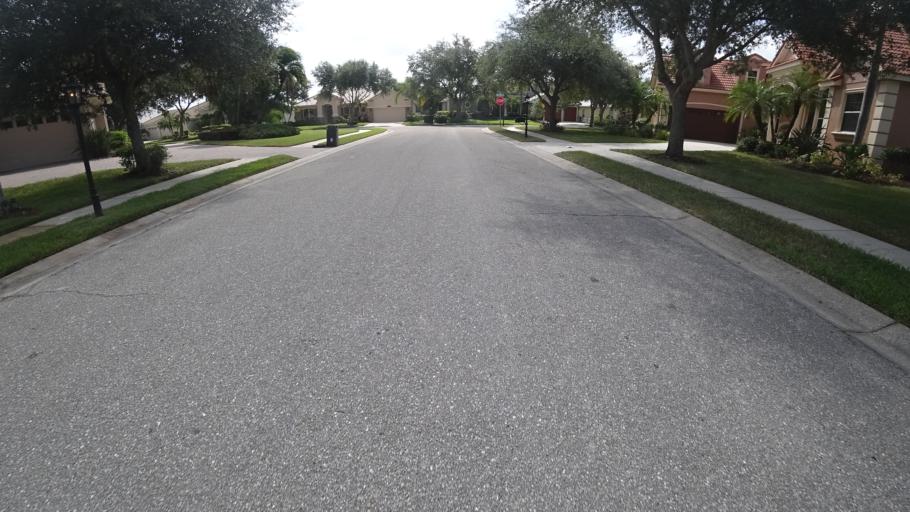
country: US
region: Florida
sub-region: Sarasota County
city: The Meadows
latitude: 27.4025
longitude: -82.4454
